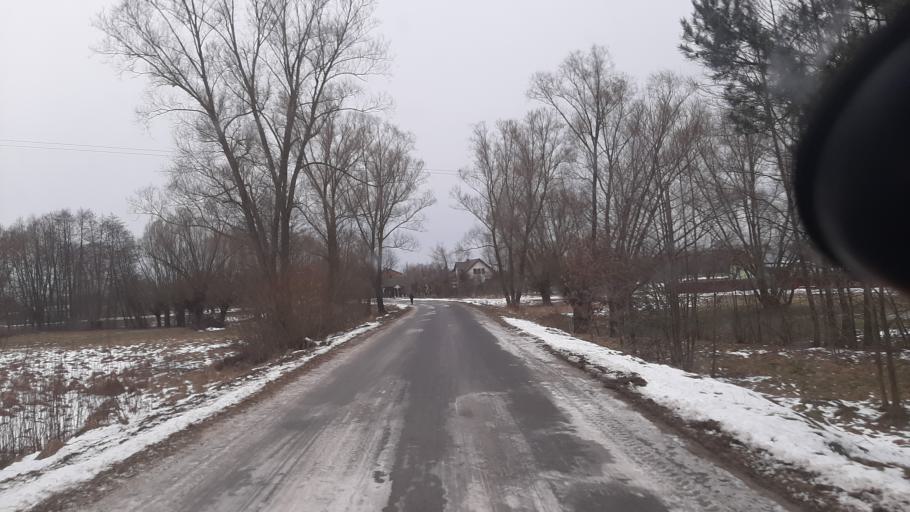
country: PL
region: Lublin Voivodeship
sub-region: Powiat lubartowski
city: Kamionka
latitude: 51.5175
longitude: 22.4769
